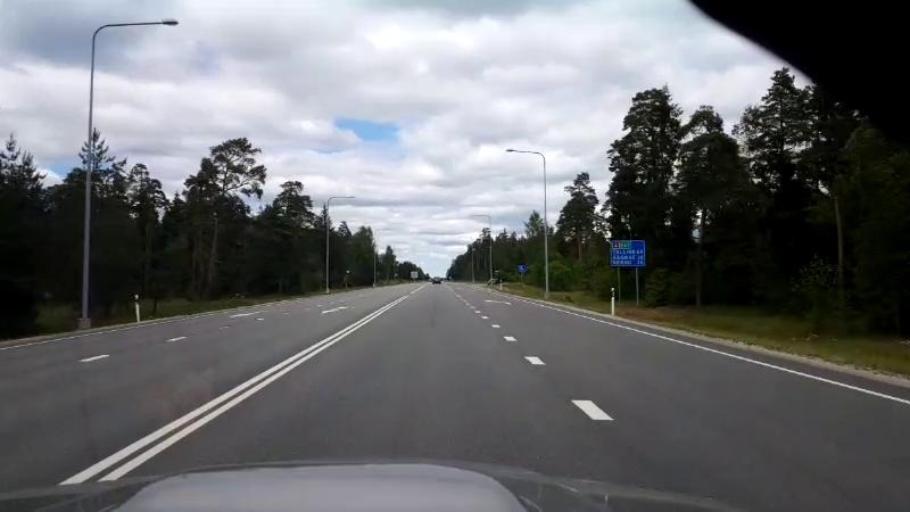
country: EE
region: Raplamaa
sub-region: Maerjamaa vald
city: Marjamaa
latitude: 58.9310
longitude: 24.4624
